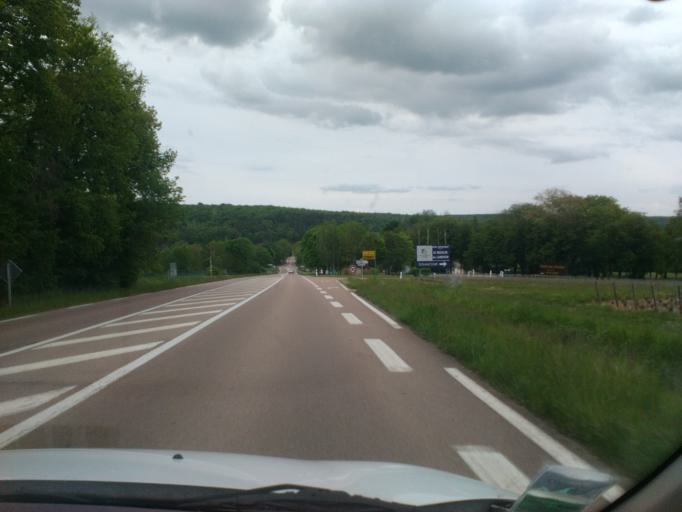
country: FR
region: Champagne-Ardenne
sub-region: Departement de l'Aube
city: Bar-sur-Aube
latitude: 48.2686
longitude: 4.6128
